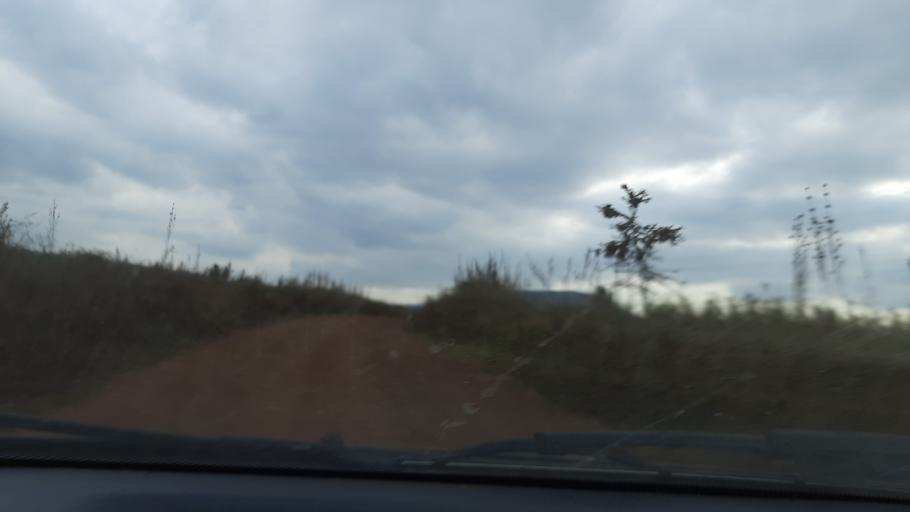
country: TZ
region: Arusha
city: Kingori
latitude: -2.8479
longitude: 37.2187
